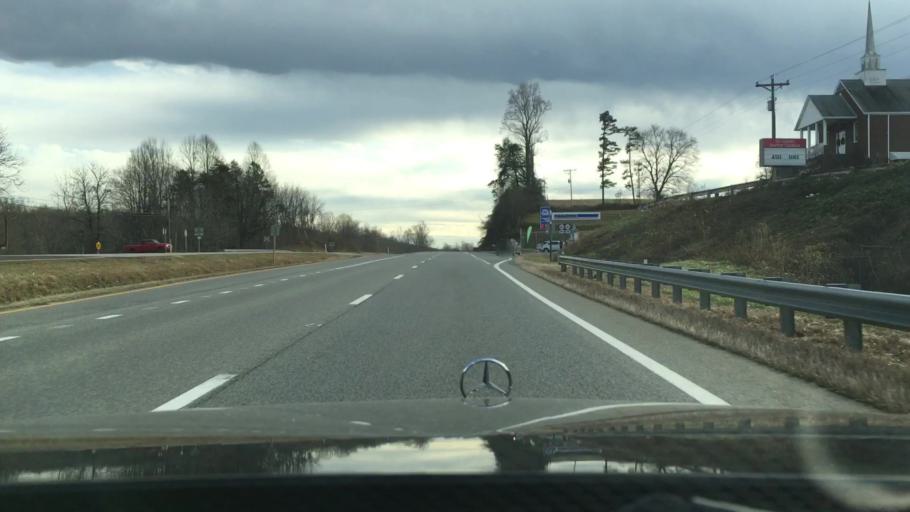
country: US
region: Virginia
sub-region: Pittsylvania County
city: Motley
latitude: 37.0252
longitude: -79.3585
